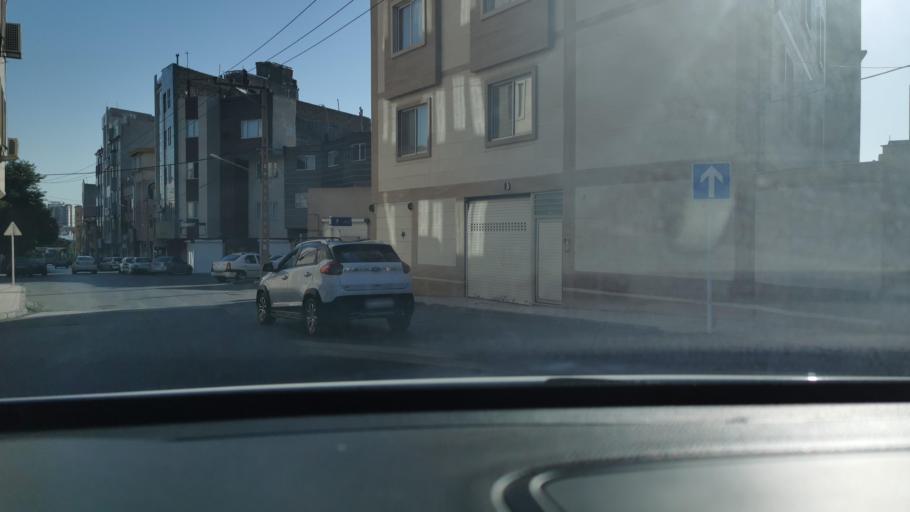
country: IR
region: Razavi Khorasan
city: Mashhad
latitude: 36.3080
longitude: 59.5108
